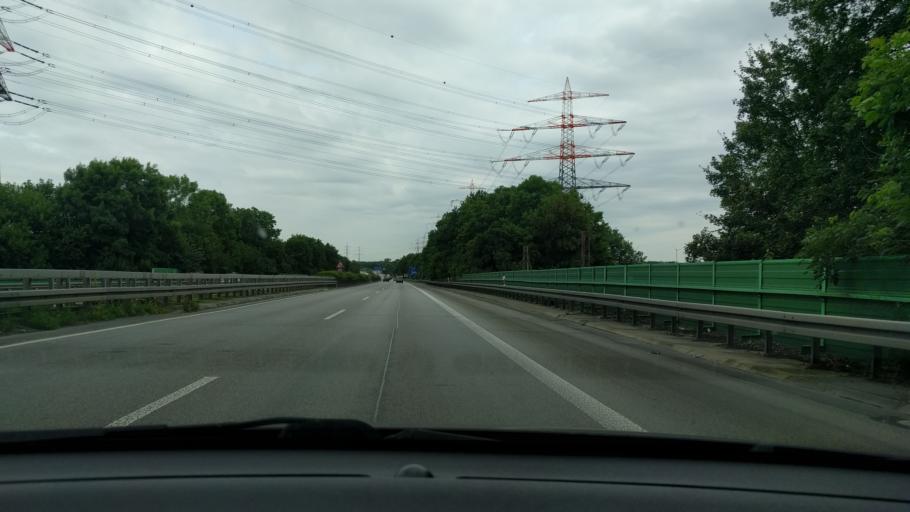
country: DE
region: North Rhine-Westphalia
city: Castrop-Rauxel
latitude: 51.5719
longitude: 7.3631
